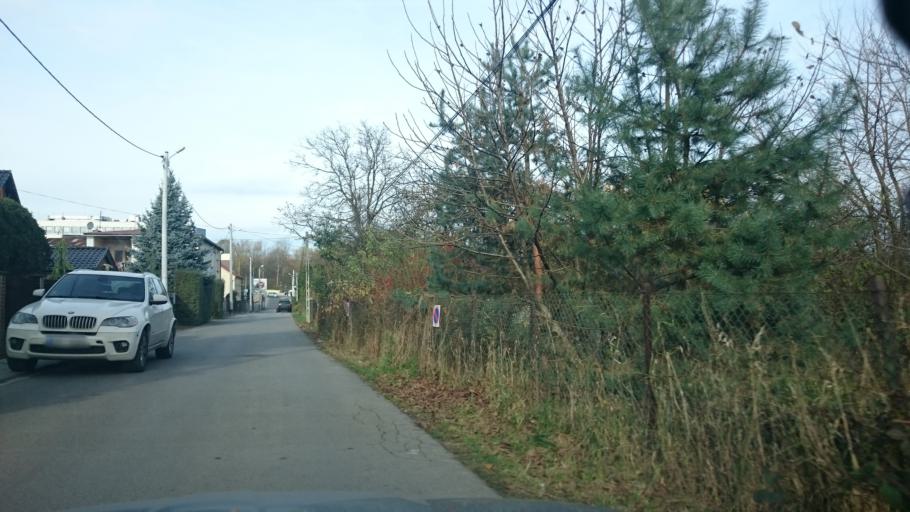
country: PL
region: Lesser Poland Voivodeship
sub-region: Krakow
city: Krakow
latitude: 50.0255
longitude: 19.9648
